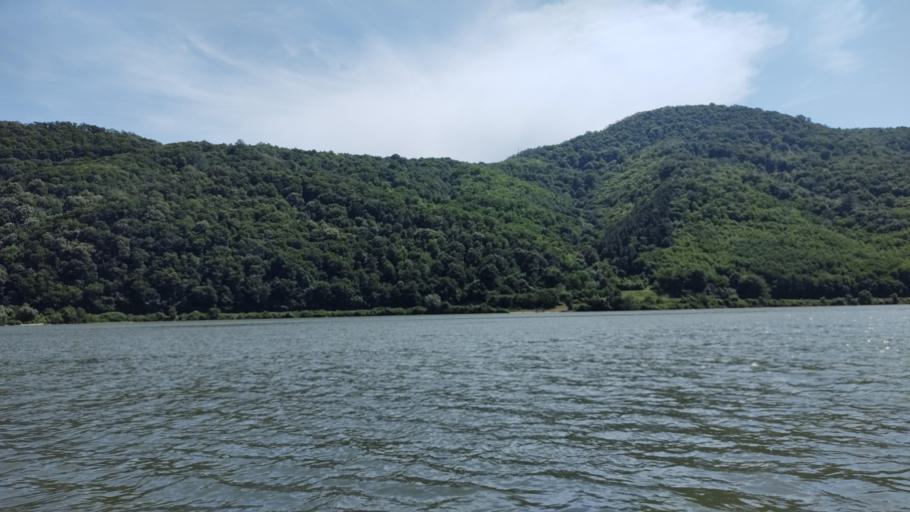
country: RO
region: Caras-Severin
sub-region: Comuna Pescari
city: Coronini
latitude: 44.6578
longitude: 21.7525
